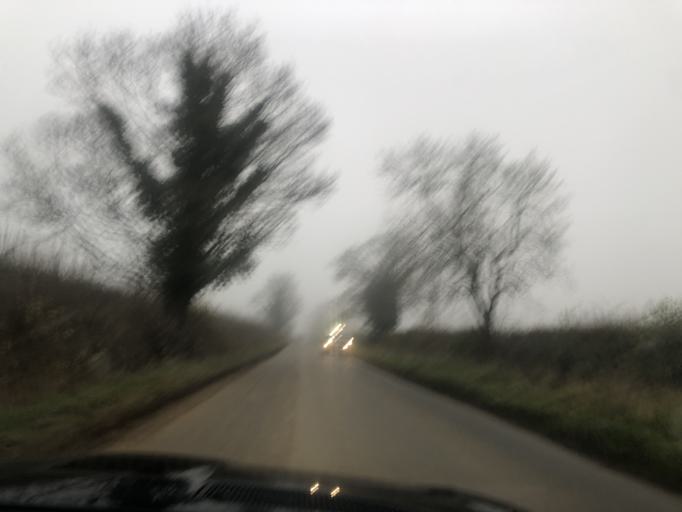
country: GB
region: England
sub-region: Oxfordshire
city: Bicester
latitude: 51.9137
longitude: -1.1730
